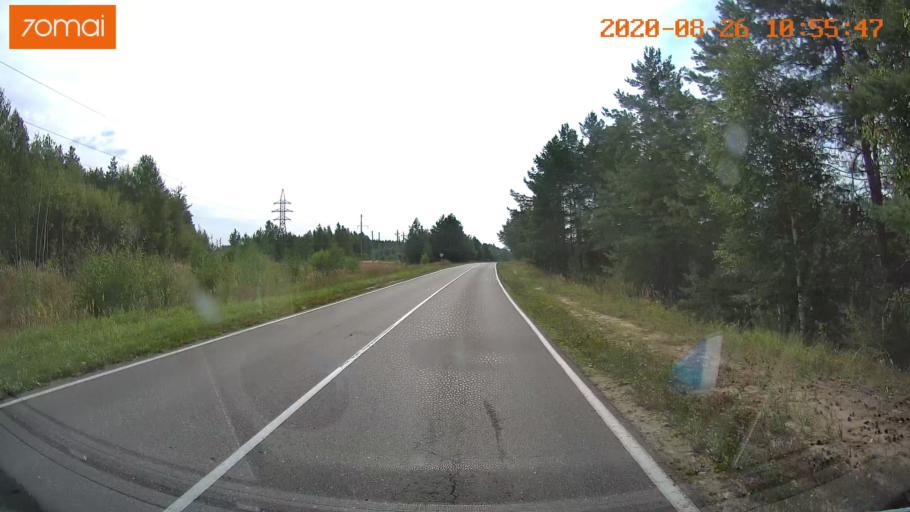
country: RU
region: Rjazan
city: Izhevskoye
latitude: 54.6123
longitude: 41.1810
